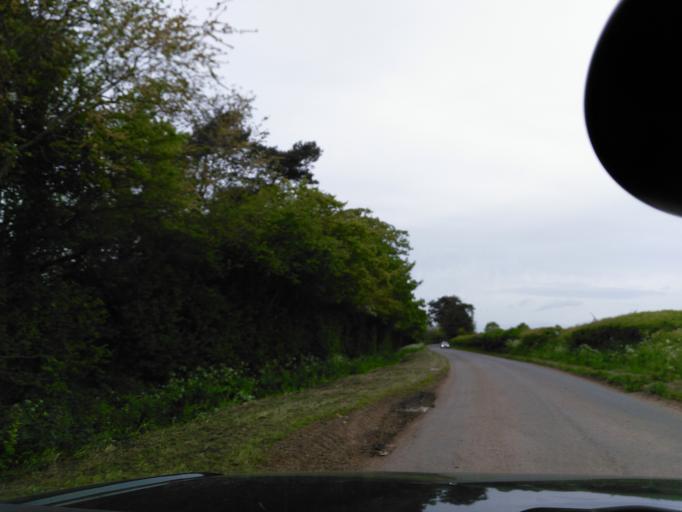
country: GB
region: England
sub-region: Wiltshire
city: Lacock
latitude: 51.4260
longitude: -2.1480
